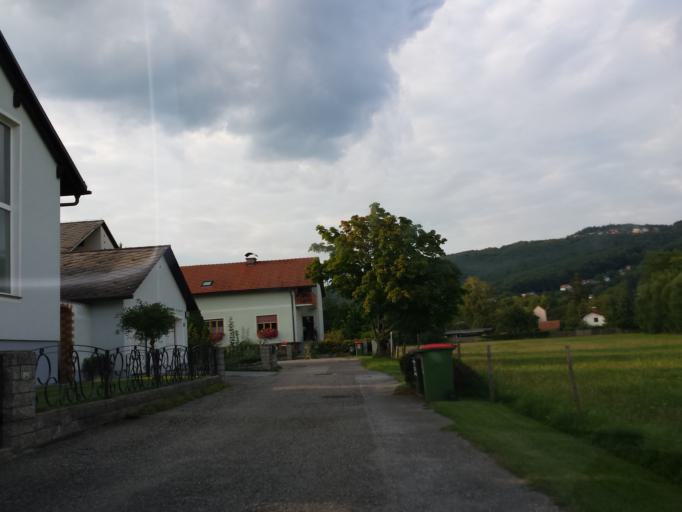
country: AT
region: Styria
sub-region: Politischer Bezirk Graz-Umgebung
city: Stattegg
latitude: 47.1242
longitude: 15.4260
